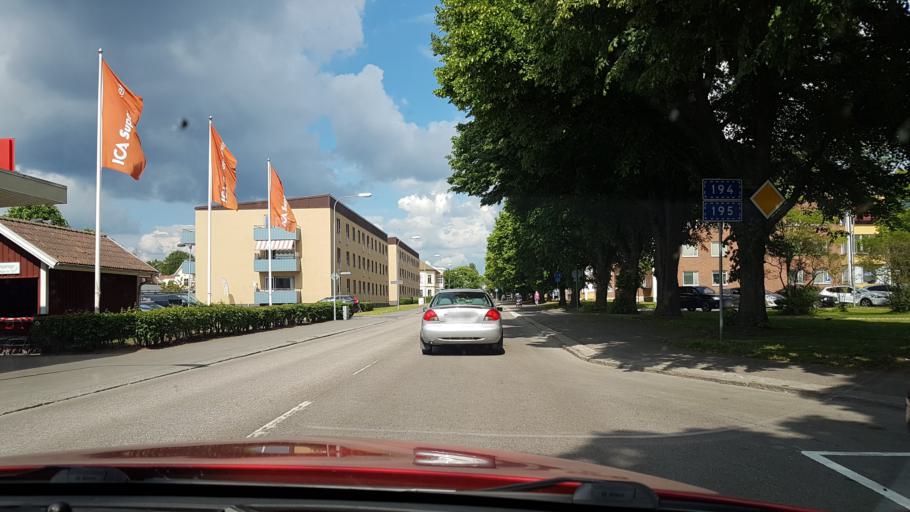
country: SE
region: Vaestra Goetaland
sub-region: Hjo Kommun
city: Hjo
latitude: 58.3048
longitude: 14.2913
